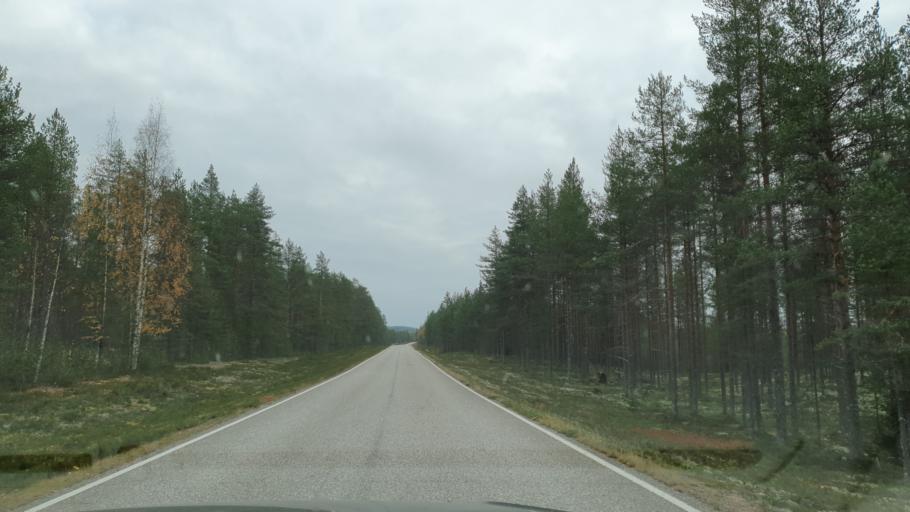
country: FI
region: Kainuu
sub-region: Kajaani
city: Paltamo
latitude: 64.6413
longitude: 27.9723
